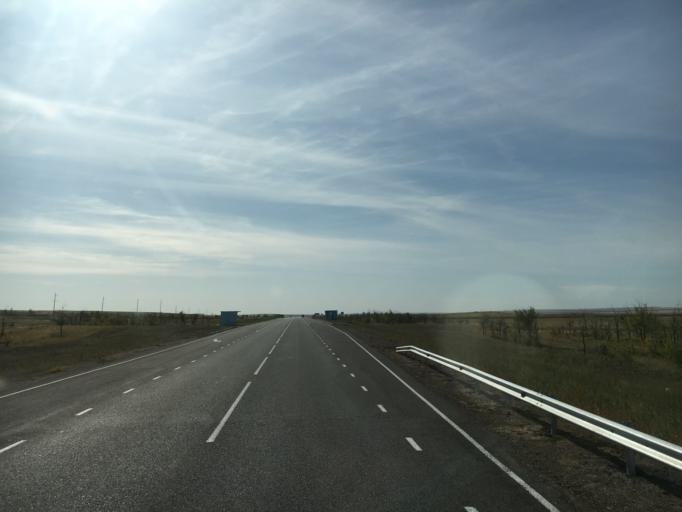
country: KZ
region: Batys Qazaqstan
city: Kamenka
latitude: 51.1136
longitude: 50.4995
